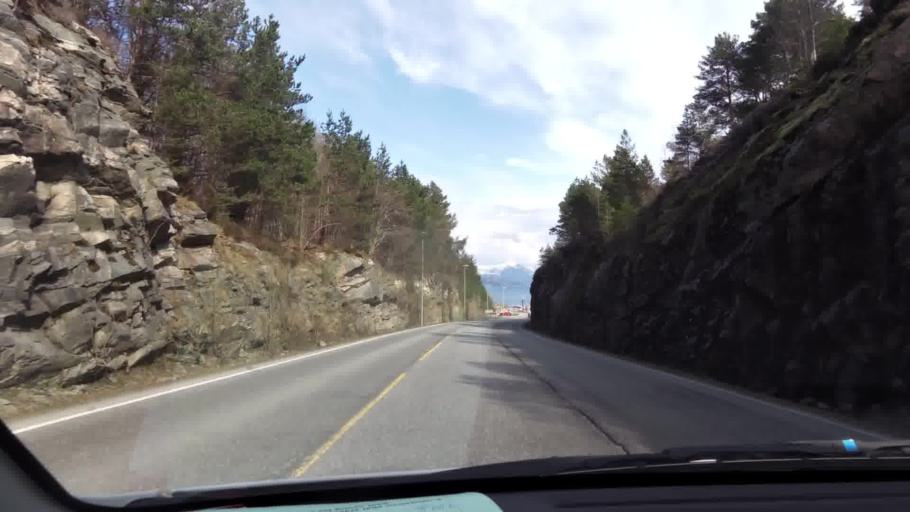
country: NO
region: More og Romsdal
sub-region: Kristiansund
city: Rensvik
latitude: 63.1109
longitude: 7.8645
